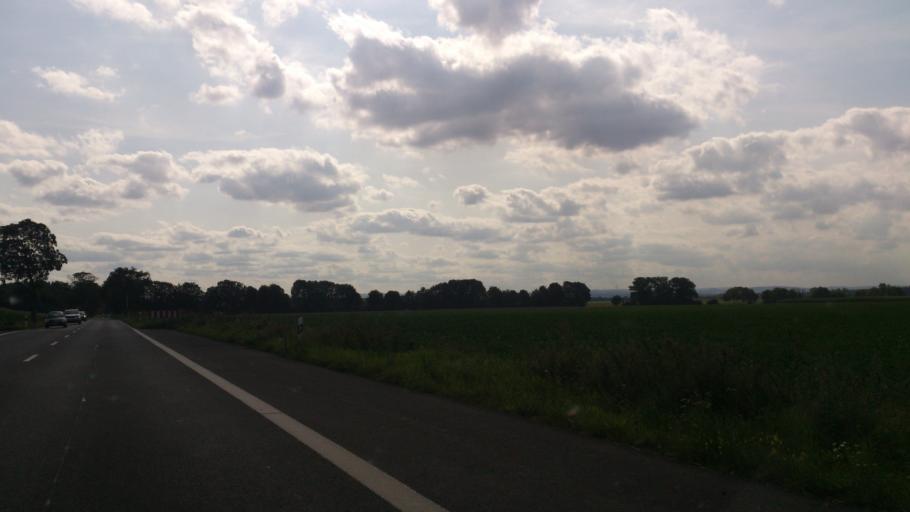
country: DE
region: North Rhine-Westphalia
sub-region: Regierungsbezirk Koln
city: Norvenich
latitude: 50.7519
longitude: 6.7144
